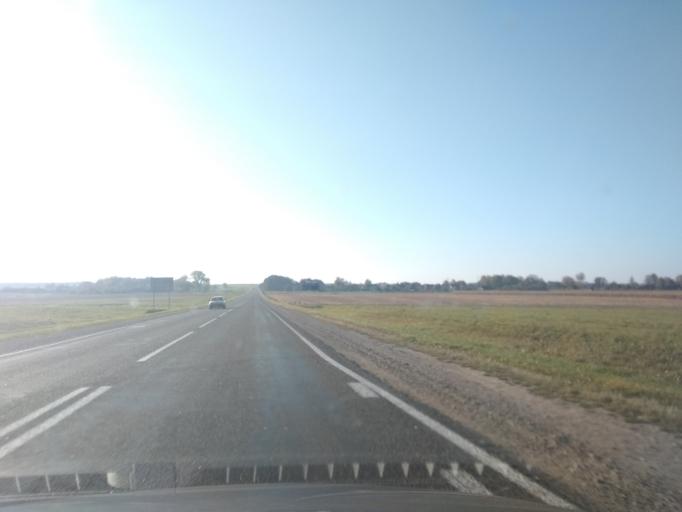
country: BY
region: Grodnenskaya
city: Svislach
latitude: 53.1329
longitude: 24.2124
